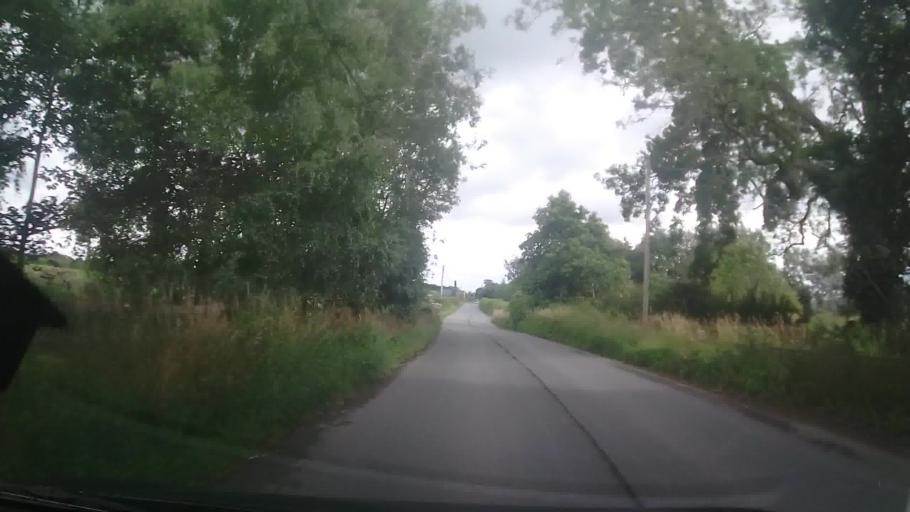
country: GB
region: England
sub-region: Shropshire
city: Whitchurch
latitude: 52.9514
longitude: -2.7368
